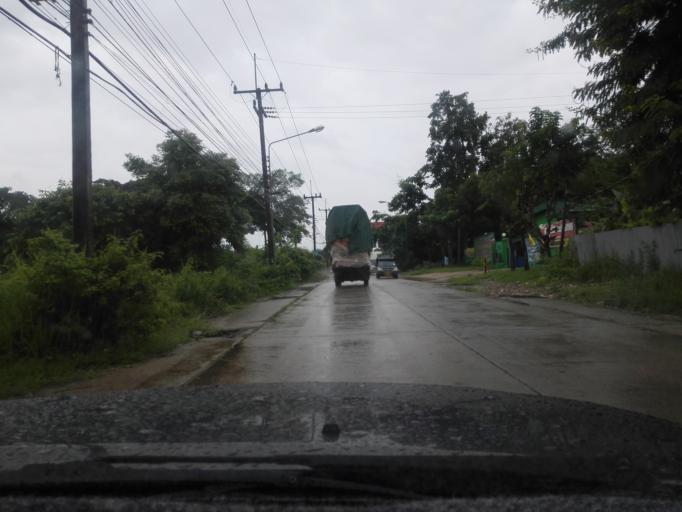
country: TH
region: Tak
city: Mae Sot
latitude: 16.6964
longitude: 98.5740
